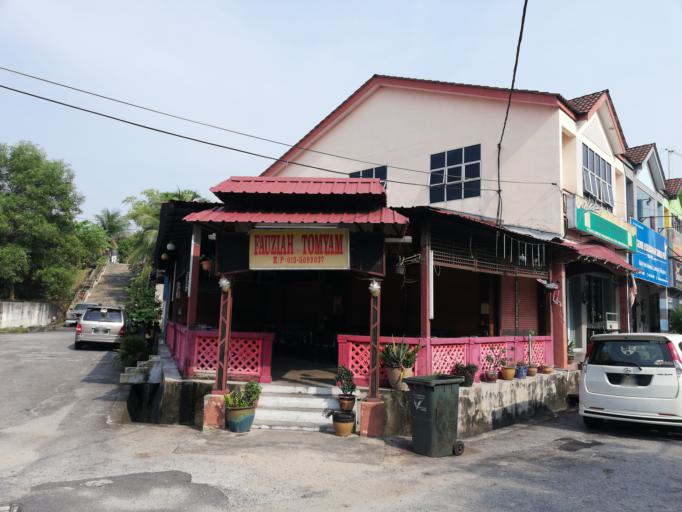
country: MY
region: Kedah
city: Kulim
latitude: 5.3732
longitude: 100.5405
